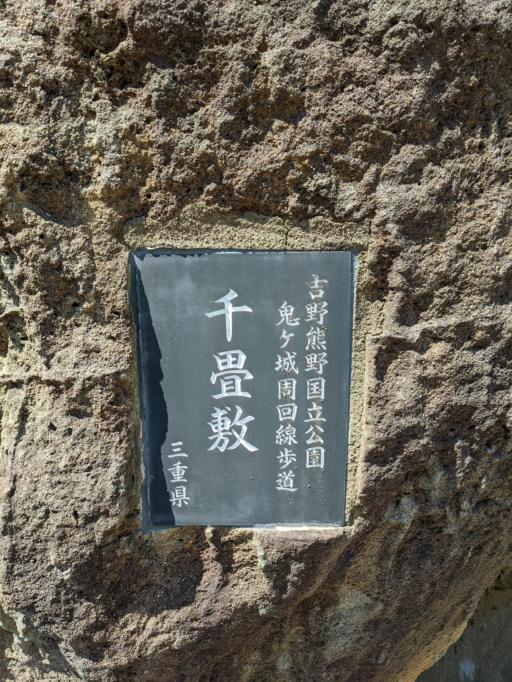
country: JP
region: Mie
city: Owase
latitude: 33.8905
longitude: 136.1163
